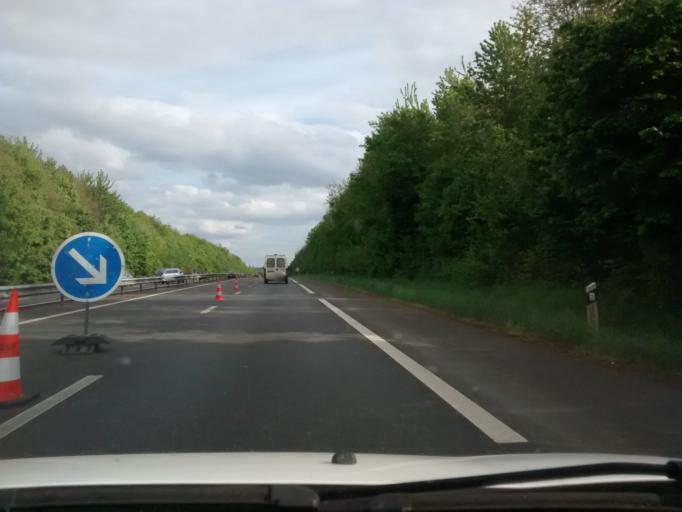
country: FR
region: Brittany
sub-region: Departement d'Ille-et-Vilaine
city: Tinteniac
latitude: 48.3211
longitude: -1.8479
